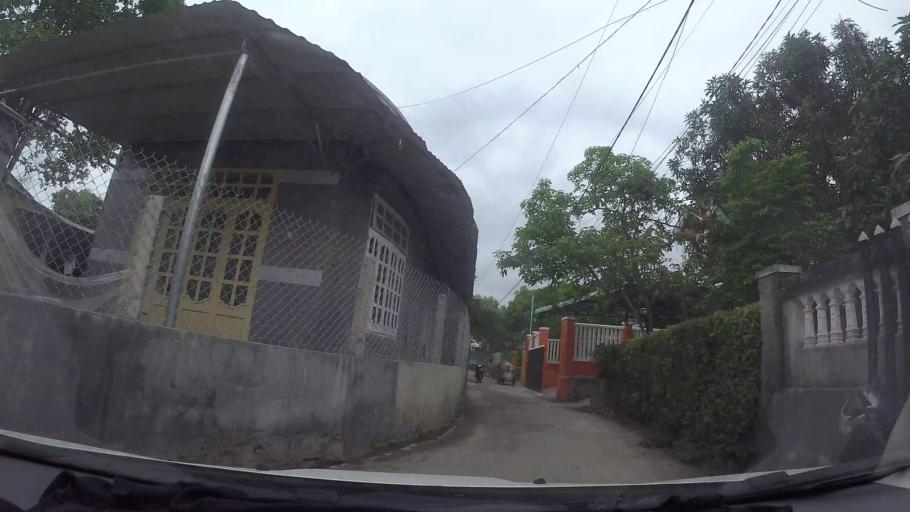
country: VN
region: Da Nang
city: Lien Chieu
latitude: 16.0776
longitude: 108.0969
